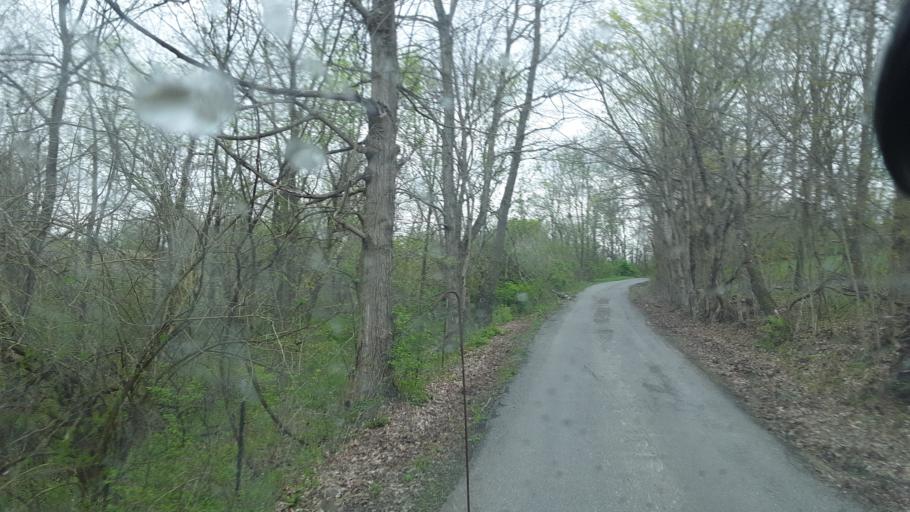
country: US
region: Kentucky
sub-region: Owen County
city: Owenton
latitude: 38.6417
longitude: -84.7768
